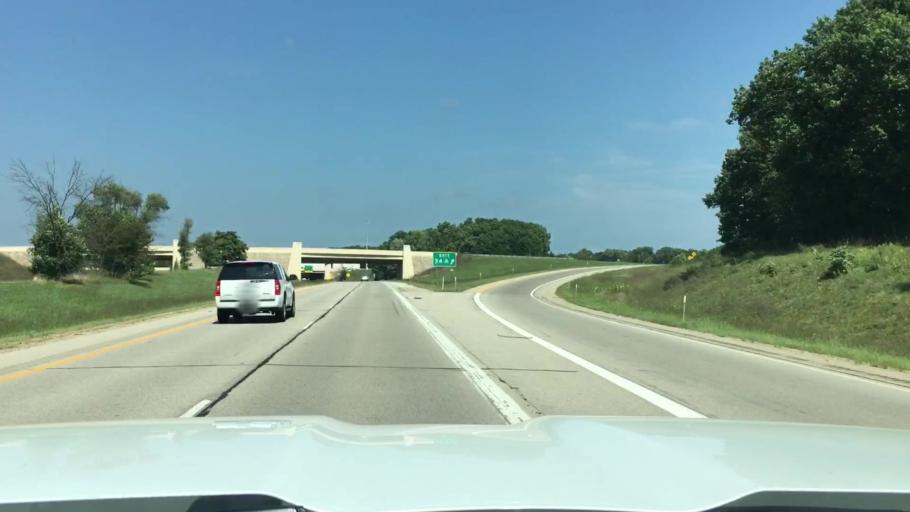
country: US
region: Michigan
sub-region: Kalamazoo County
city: Portage
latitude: 42.2334
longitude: -85.6378
